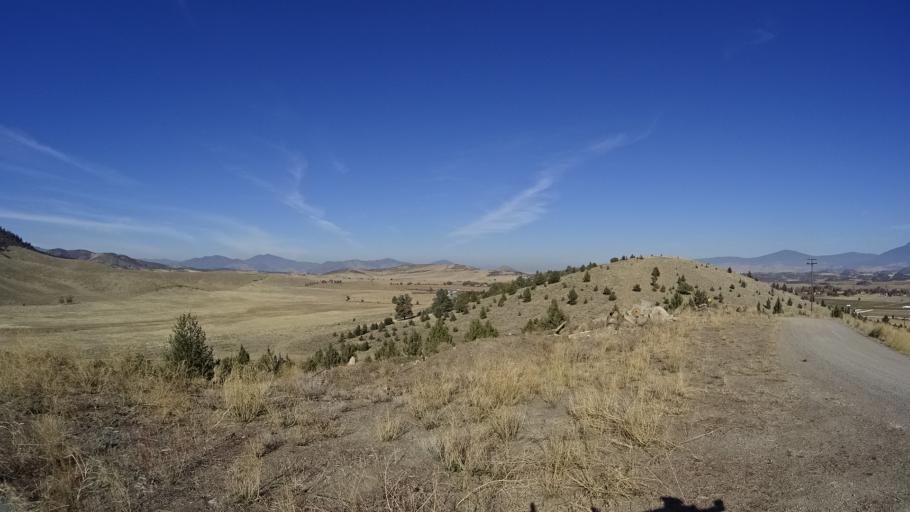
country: US
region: California
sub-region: Siskiyou County
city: Montague
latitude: 41.6358
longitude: -122.5404
